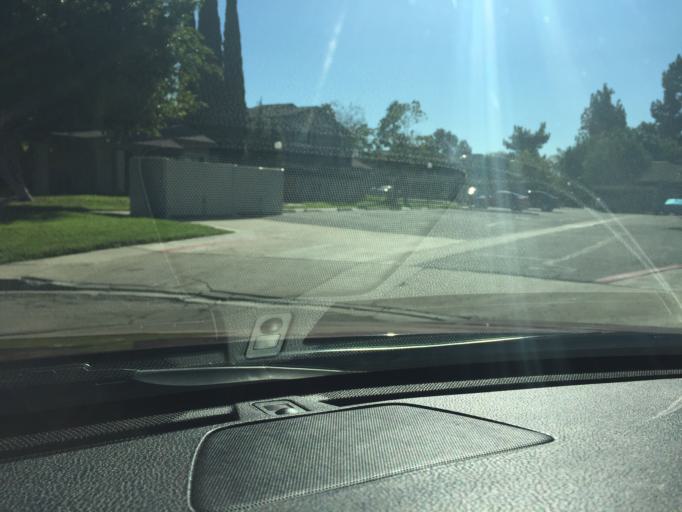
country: US
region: California
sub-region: San Diego County
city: La Mesa
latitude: 32.8222
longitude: -117.0954
